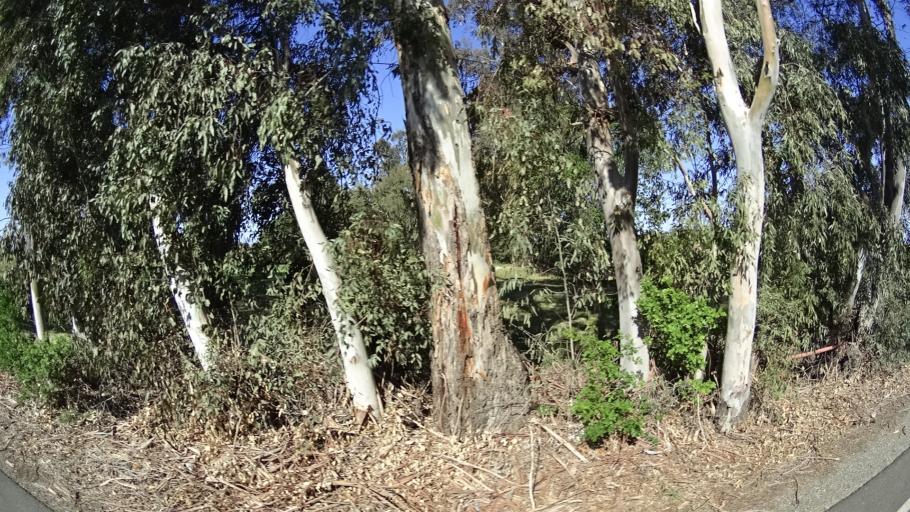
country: US
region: California
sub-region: Glenn County
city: Orland
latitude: 39.7510
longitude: -122.1410
